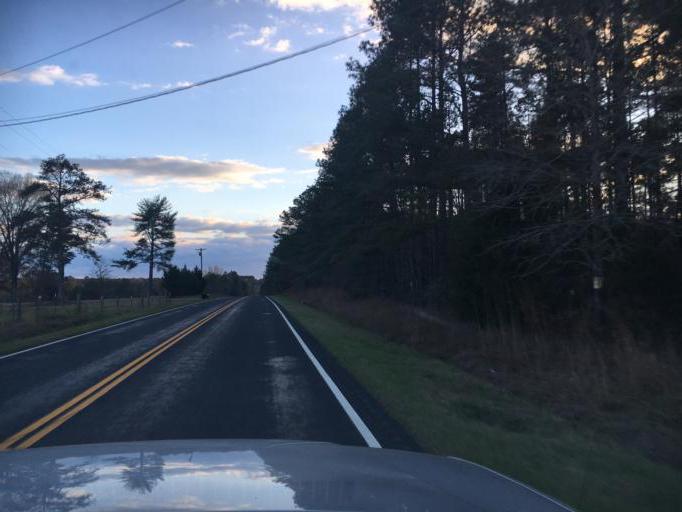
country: US
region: South Carolina
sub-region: Greenwood County
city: Greenwood
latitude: 34.0665
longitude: -82.2284
